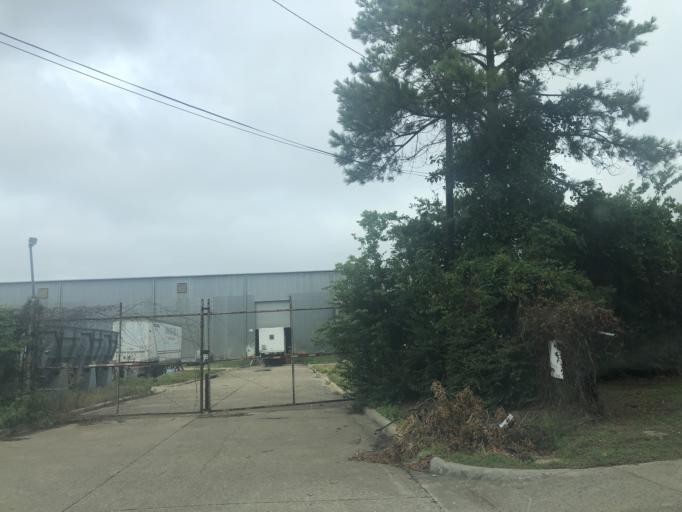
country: US
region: Texas
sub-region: Dallas County
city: Dallas
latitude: 32.7763
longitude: -96.8514
